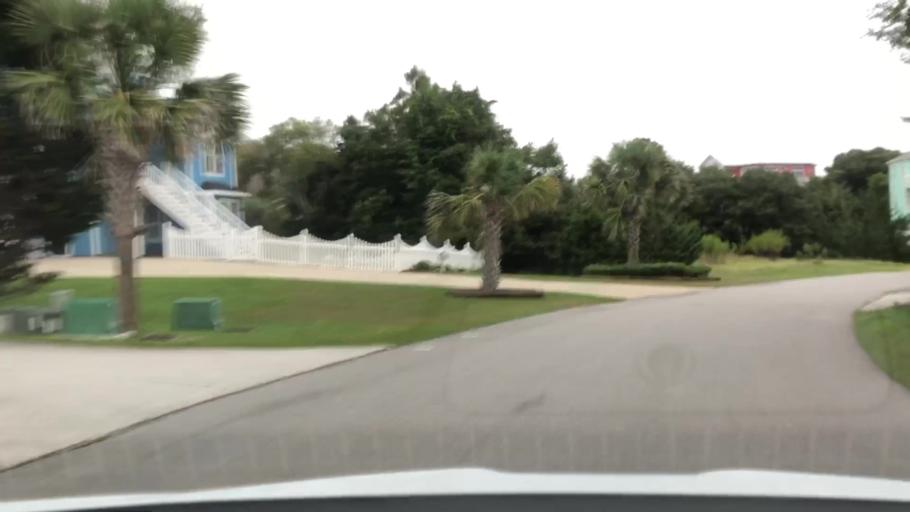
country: US
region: North Carolina
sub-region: Carteret County
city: Cedar Point
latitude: 34.6518
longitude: -77.0775
